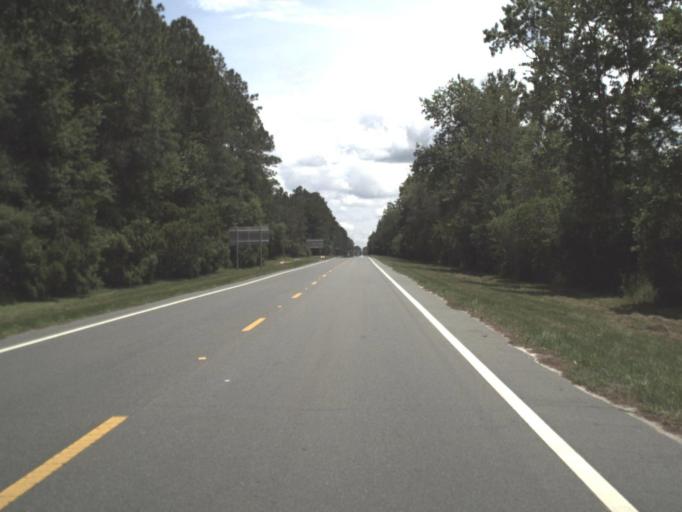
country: US
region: Georgia
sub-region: Camden County
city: Kingsland
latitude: 30.7287
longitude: -81.6848
